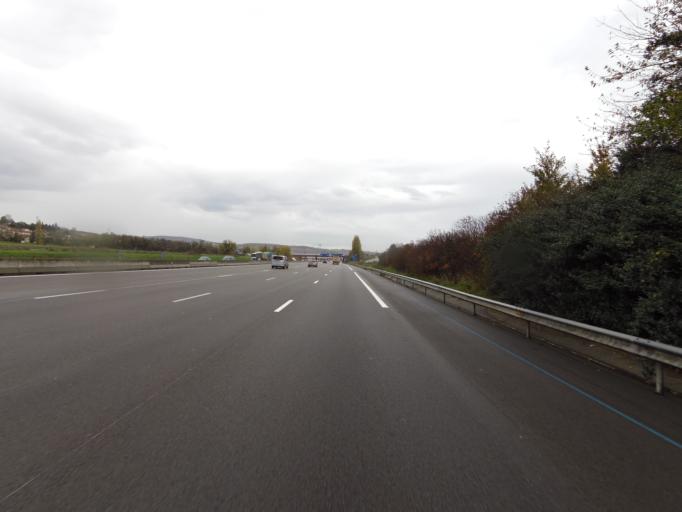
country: FR
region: Rhone-Alpes
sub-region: Departement de l'Isere
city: Reventin-Vaugris
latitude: 45.4694
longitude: 4.8334
